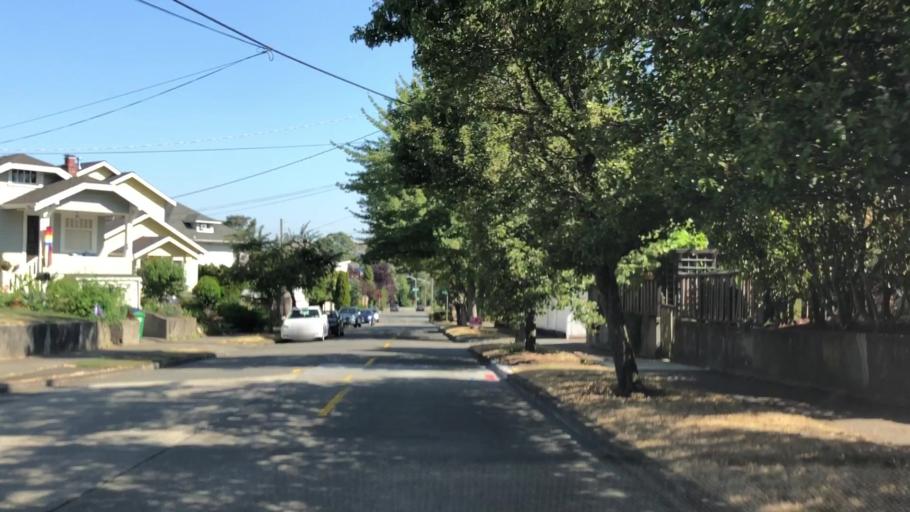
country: US
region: Washington
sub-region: King County
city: Seattle
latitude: 47.6730
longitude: -122.3335
